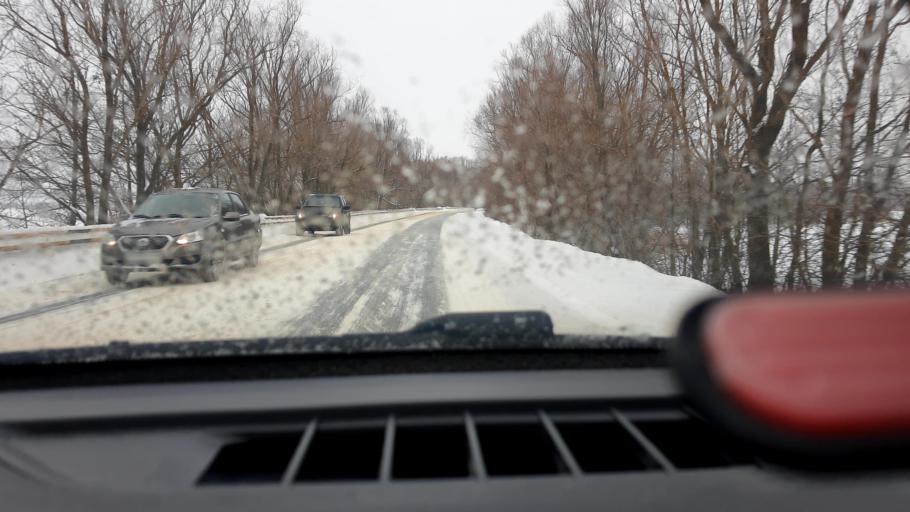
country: RU
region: Nizjnij Novgorod
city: Buturlino
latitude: 55.5718
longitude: 44.9067
